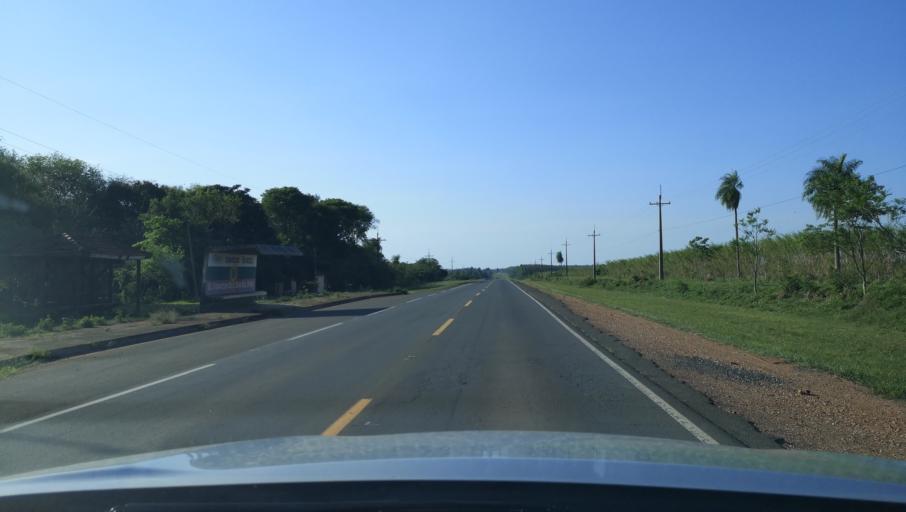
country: PY
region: Misiones
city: Santa Maria
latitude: -26.7821
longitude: -57.0273
